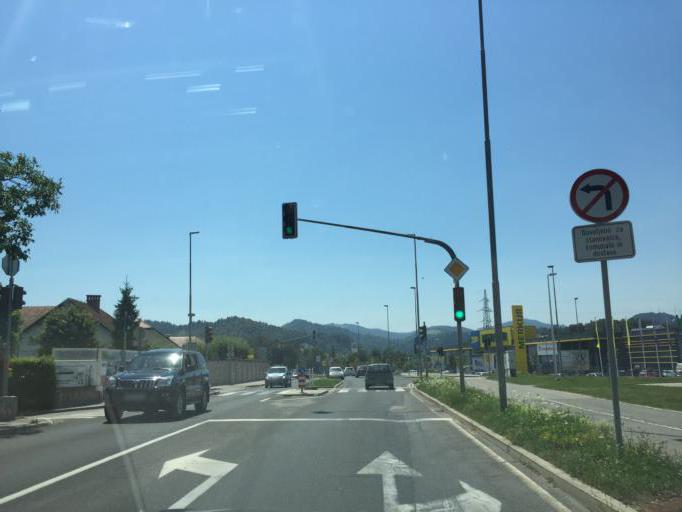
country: SI
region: Skofja Loka
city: Sv. Duh
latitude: 46.1749
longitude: 14.3217
